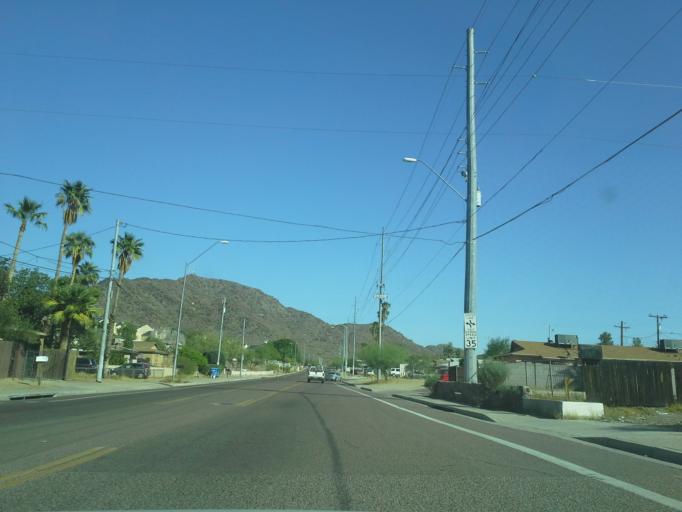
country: US
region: Arizona
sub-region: Maricopa County
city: Glendale
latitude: 33.5820
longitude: -112.0904
